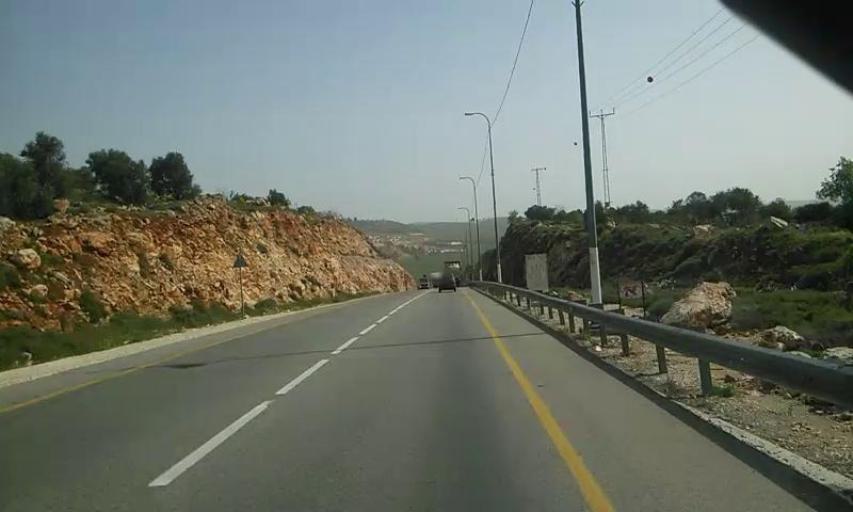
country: PS
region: West Bank
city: Turmus`ayya
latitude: 32.0468
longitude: 35.2894
